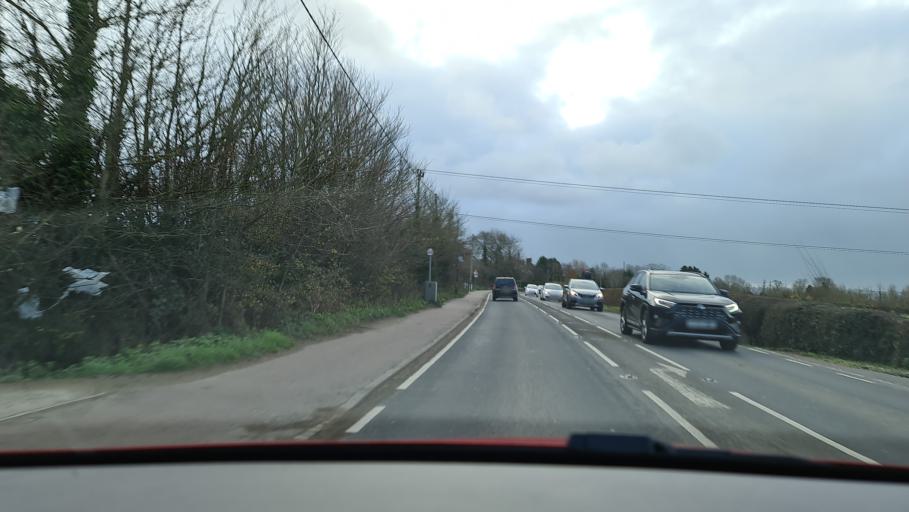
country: GB
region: England
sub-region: Buckinghamshire
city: Aylesbury
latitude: 51.7934
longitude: -0.8019
